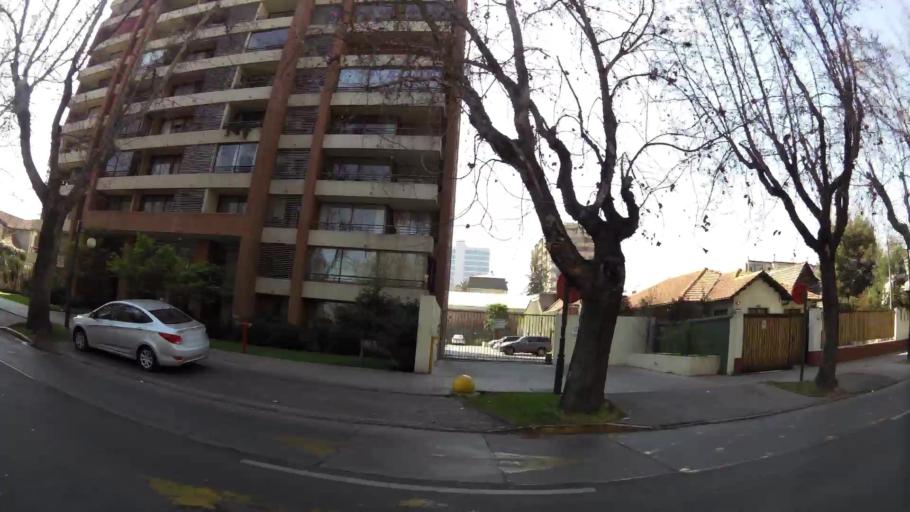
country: CL
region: Santiago Metropolitan
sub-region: Provincia de Santiago
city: Villa Presidente Frei, Nunoa, Santiago, Chile
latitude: -33.4570
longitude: -70.6066
